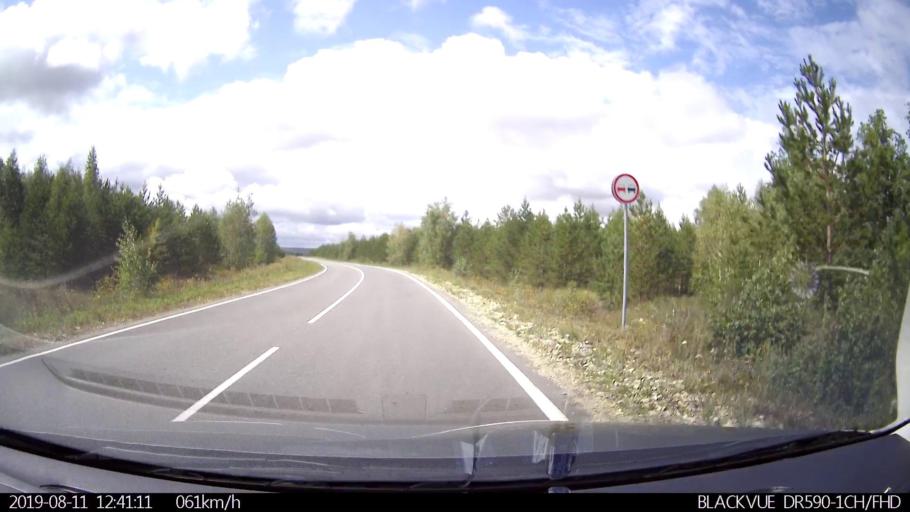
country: RU
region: Ulyanovsk
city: Ignatovka
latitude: 53.8425
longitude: 47.7702
